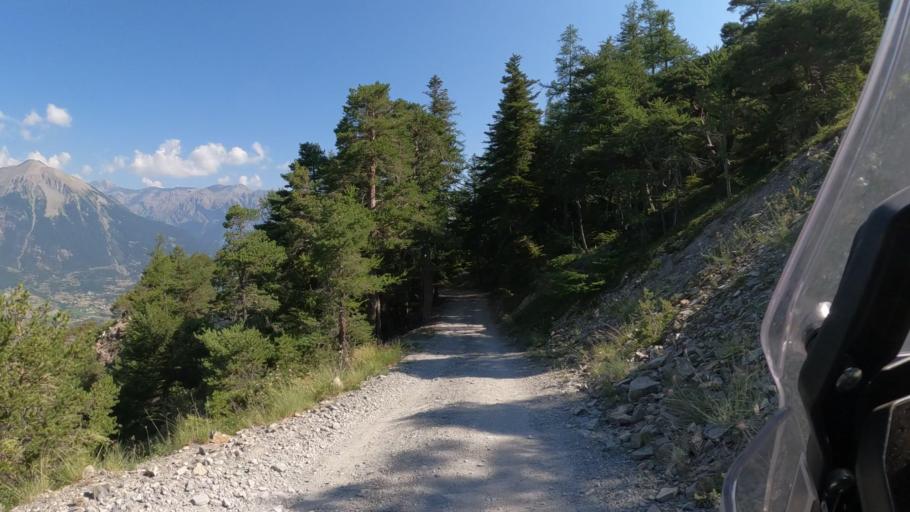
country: FR
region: Provence-Alpes-Cote d'Azur
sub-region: Departement des Hautes-Alpes
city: Embrun
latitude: 44.5999
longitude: 6.5645
